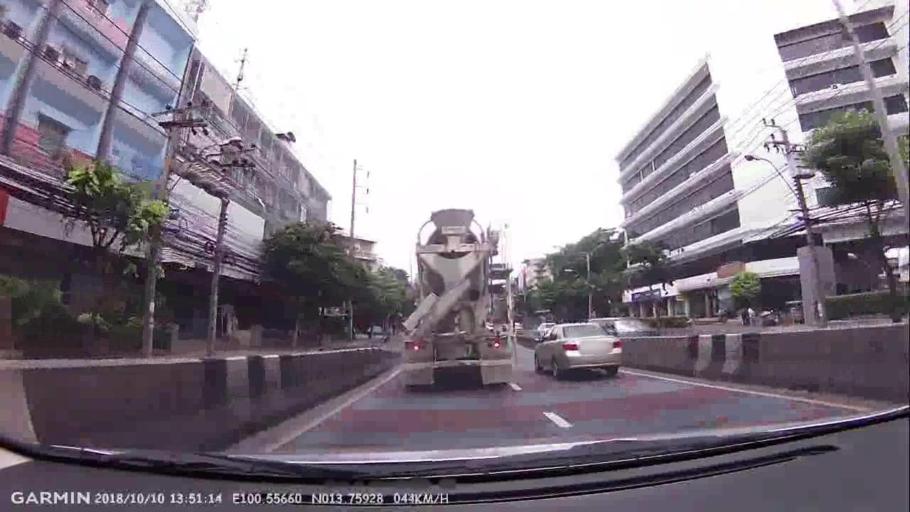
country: TH
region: Bangkok
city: Din Daeng
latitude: 13.7592
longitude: 100.5566
